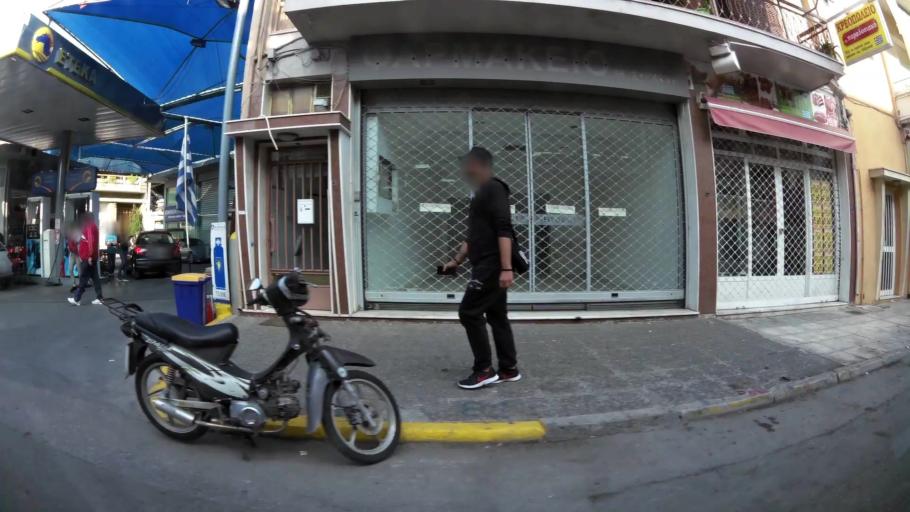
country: GR
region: Attica
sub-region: Nomarchia Anatolikis Attikis
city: Acharnes
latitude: 38.0777
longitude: 23.7390
